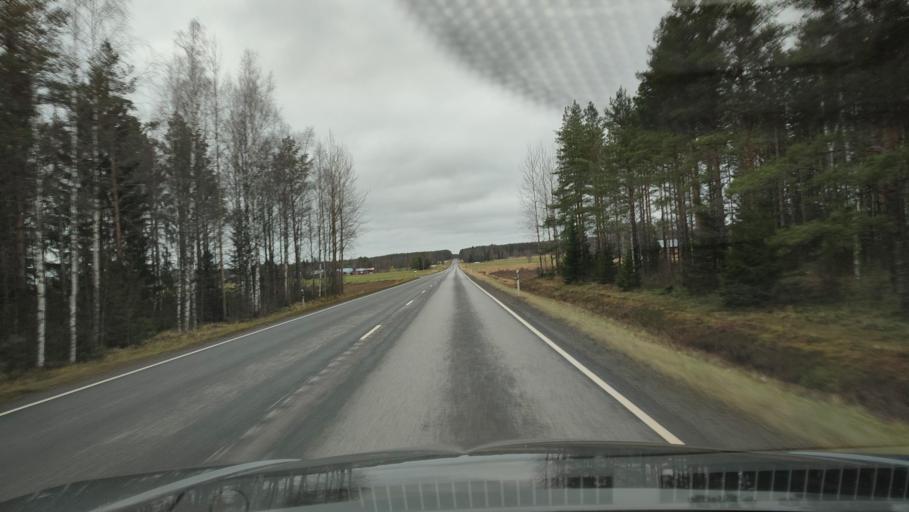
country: FI
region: Southern Ostrobothnia
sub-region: Suupohja
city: Kauhajoki
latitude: 62.4957
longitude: 22.2983
